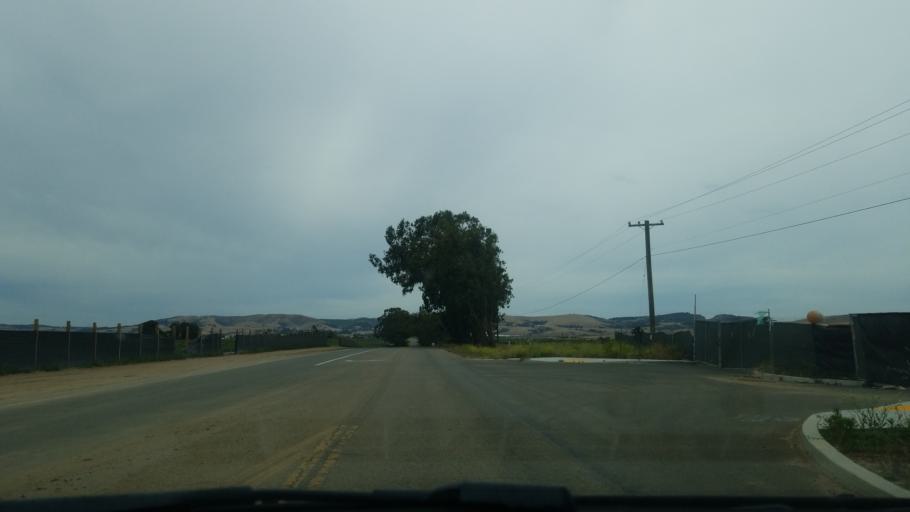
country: US
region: California
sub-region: Santa Barbara County
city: Santa Maria
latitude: 34.9186
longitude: -120.4902
